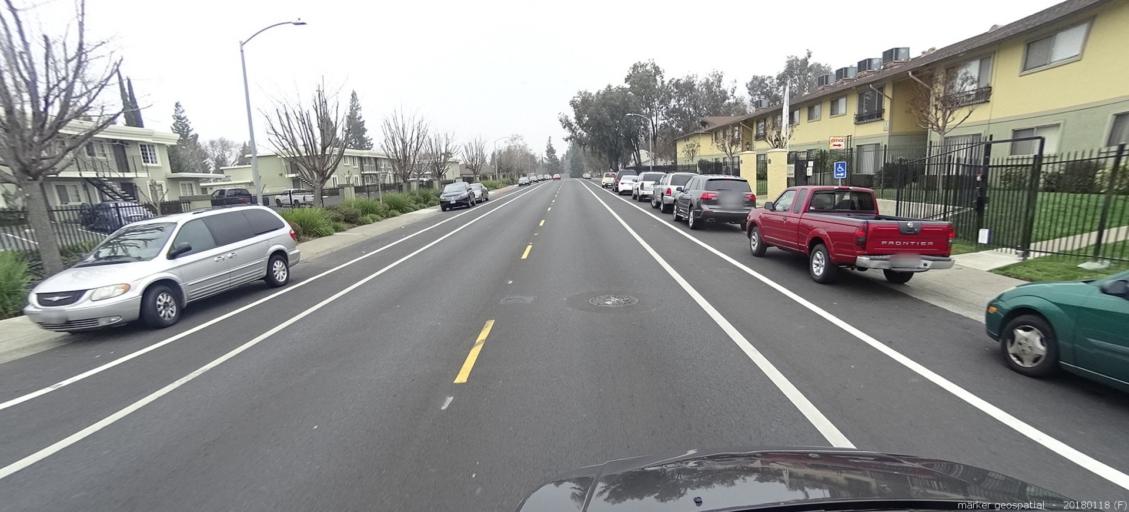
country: US
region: California
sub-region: Sacramento County
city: Rancho Cordova
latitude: 38.5830
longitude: -121.3197
